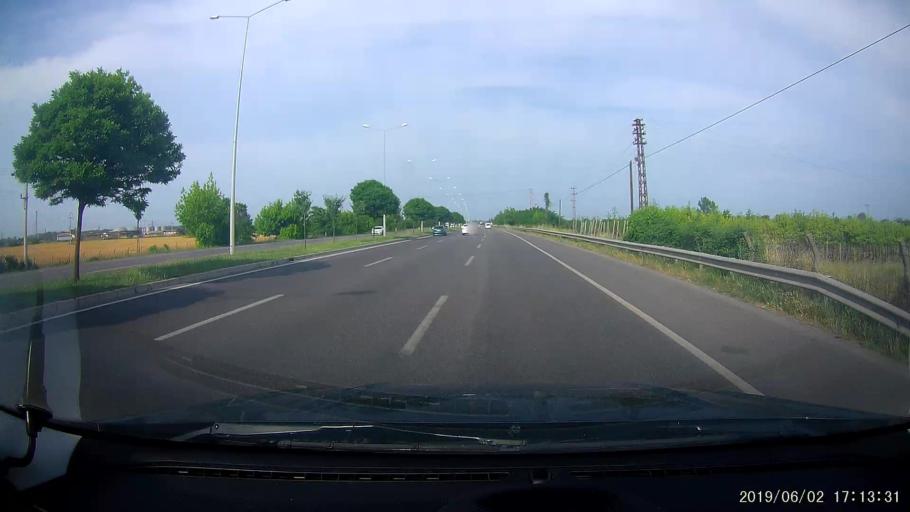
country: TR
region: Samsun
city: Tekkekoy
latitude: 41.2314
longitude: 36.5101
